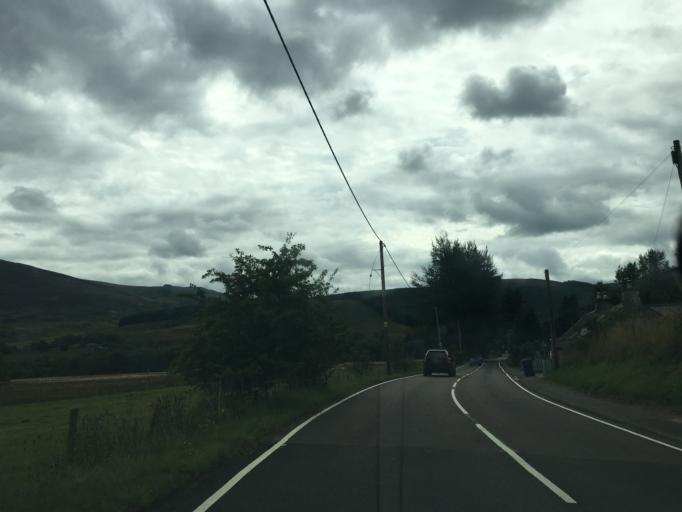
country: GB
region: Scotland
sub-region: Stirling
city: Callander
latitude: 56.3843
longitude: -4.2868
